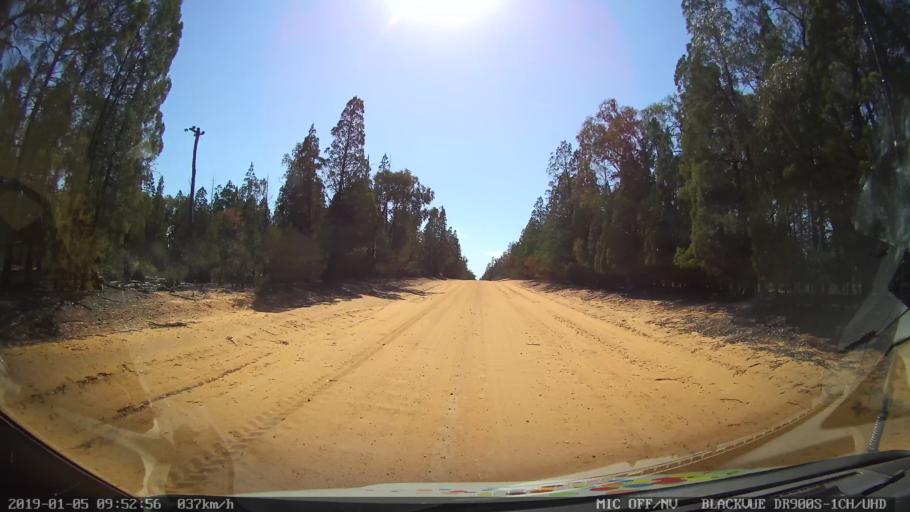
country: AU
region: New South Wales
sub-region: Gilgandra
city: Gilgandra
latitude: -31.6619
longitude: 148.7706
